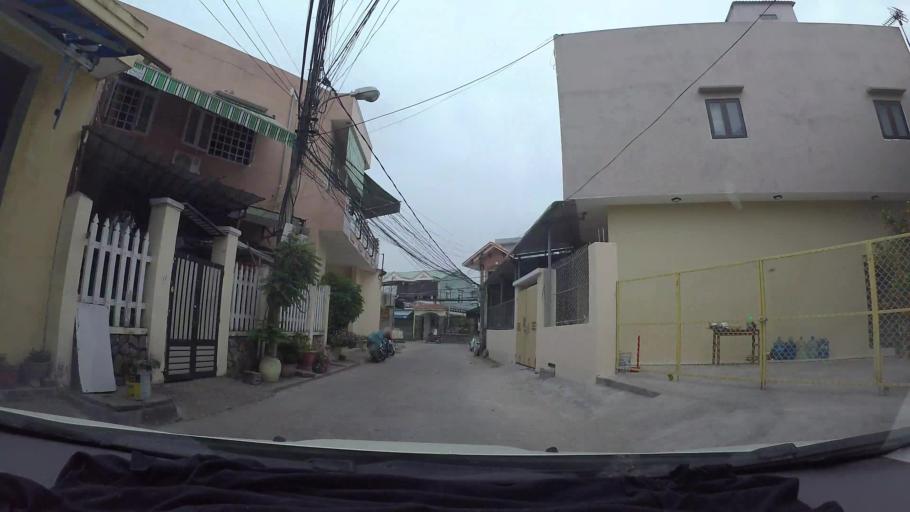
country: VN
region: Da Nang
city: Lien Chieu
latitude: 16.0748
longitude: 108.1480
